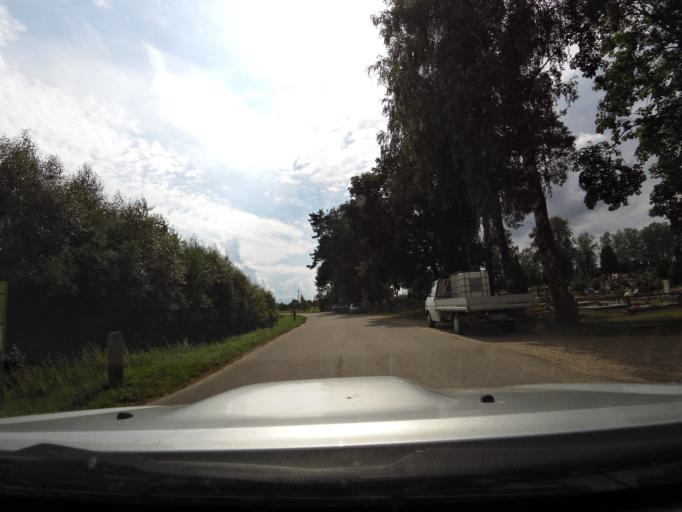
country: LT
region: Vilnius County
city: Elektrenai
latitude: 54.9115
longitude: 24.7249
